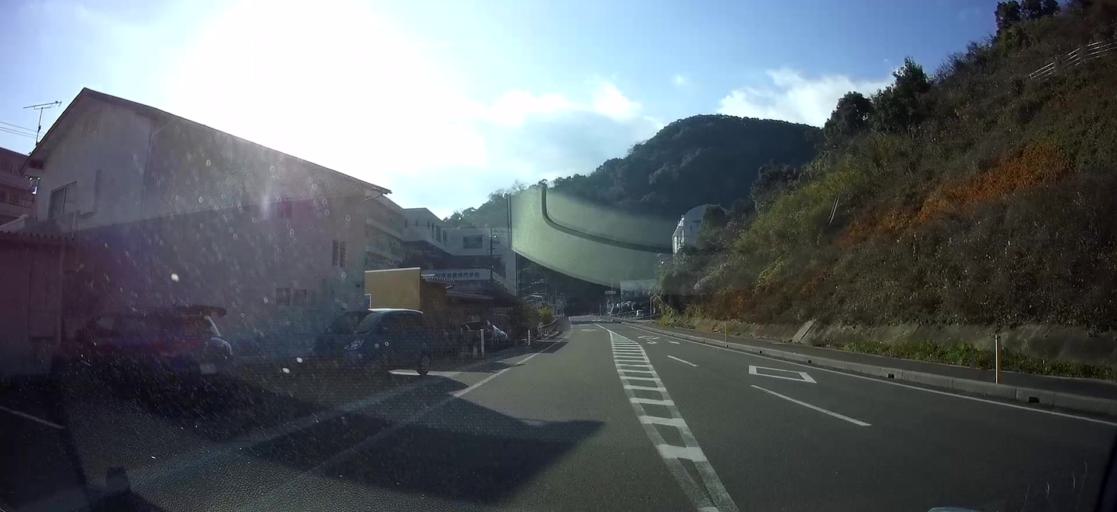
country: JP
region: Kumamoto
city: Minamata
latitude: 32.3943
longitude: 130.3910
